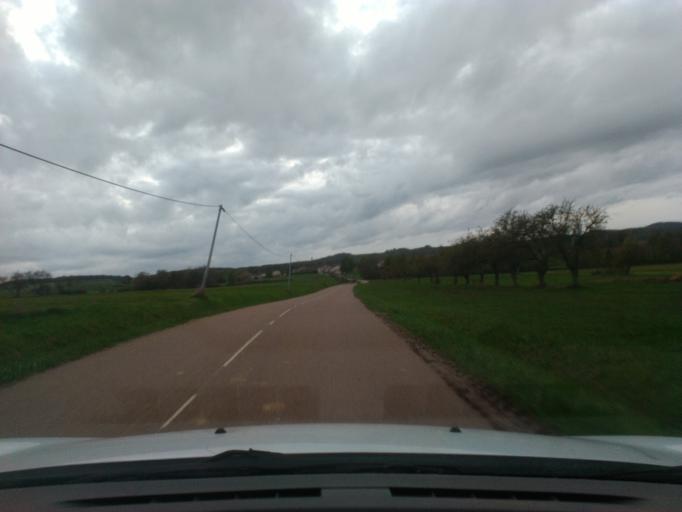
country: FR
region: Lorraine
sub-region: Departement des Vosges
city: Mirecourt
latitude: 48.3526
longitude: 6.0767
